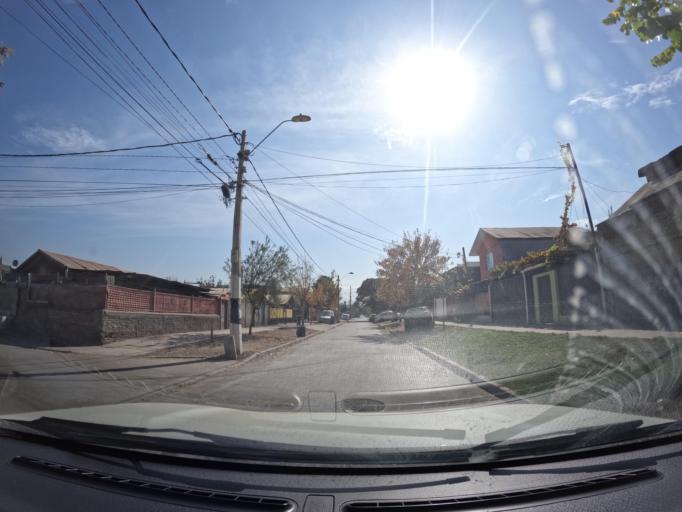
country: CL
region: Santiago Metropolitan
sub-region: Provincia de Santiago
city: Villa Presidente Frei, Nunoa, Santiago, Chile
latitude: -33.4699
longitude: -70.5542
